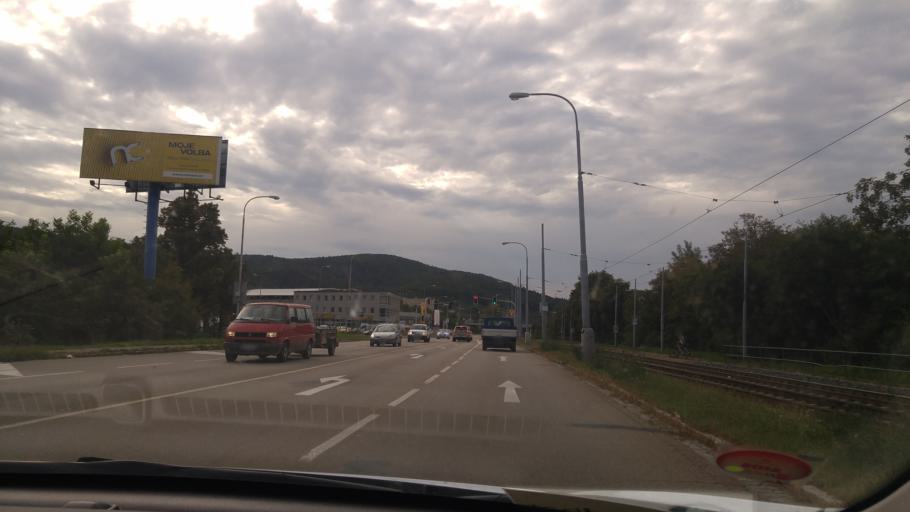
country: CZ
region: South Moravian
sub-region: Mesto Brno
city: Brno
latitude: 49.2124
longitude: 16.5644
